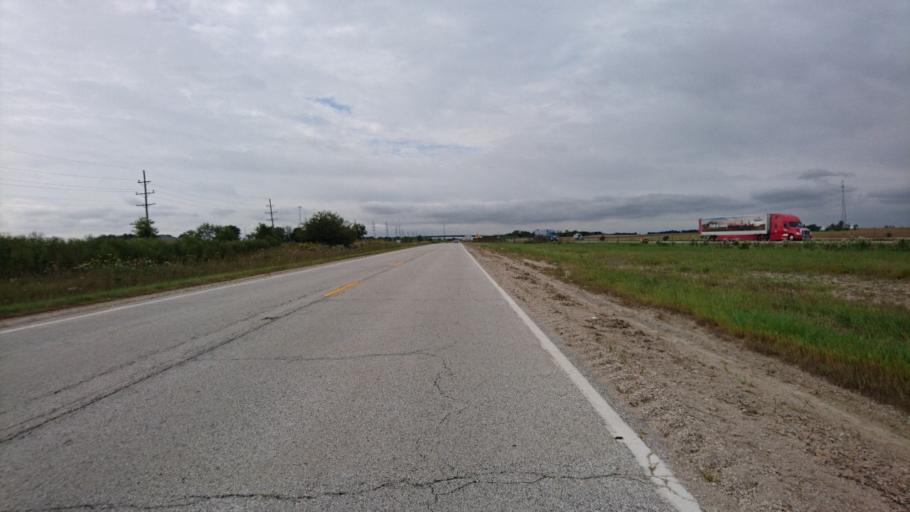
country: US
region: Illinois
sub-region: Livingston County
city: Dwight
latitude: 41.0712
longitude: -88.4551
